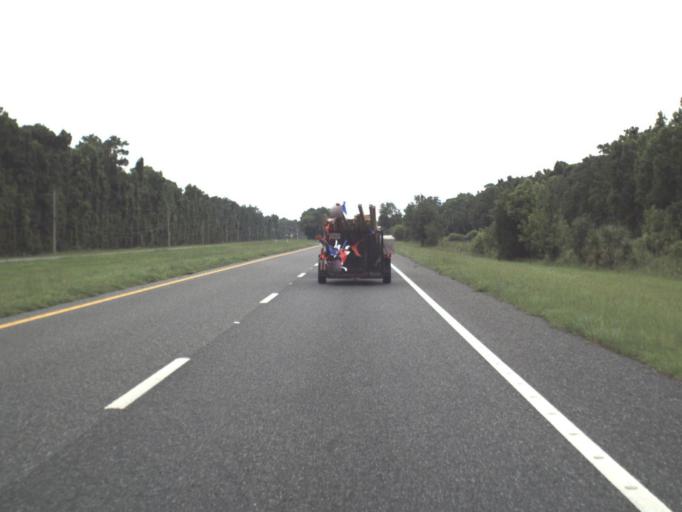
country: US
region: Florida
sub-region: Levy County
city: Williston Highlands
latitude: 29.2440
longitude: -82.7175
